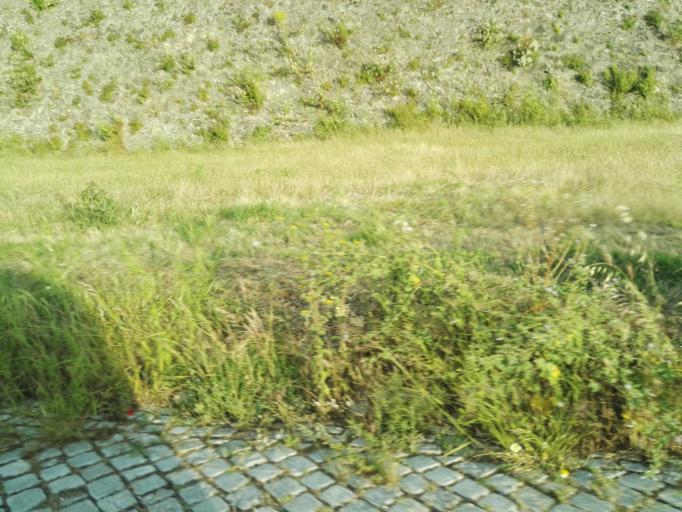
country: PT
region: Portalegre
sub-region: Elvas
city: Elvas
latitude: 38.8739
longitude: -7.1578
